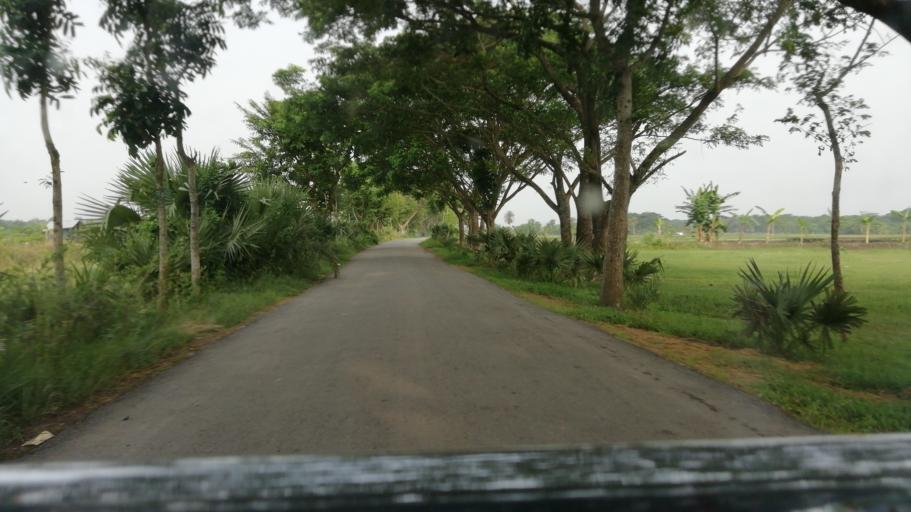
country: BD
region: Khulna
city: Bhatpara Abhaynagar
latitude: 23.0402
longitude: 89.3193
